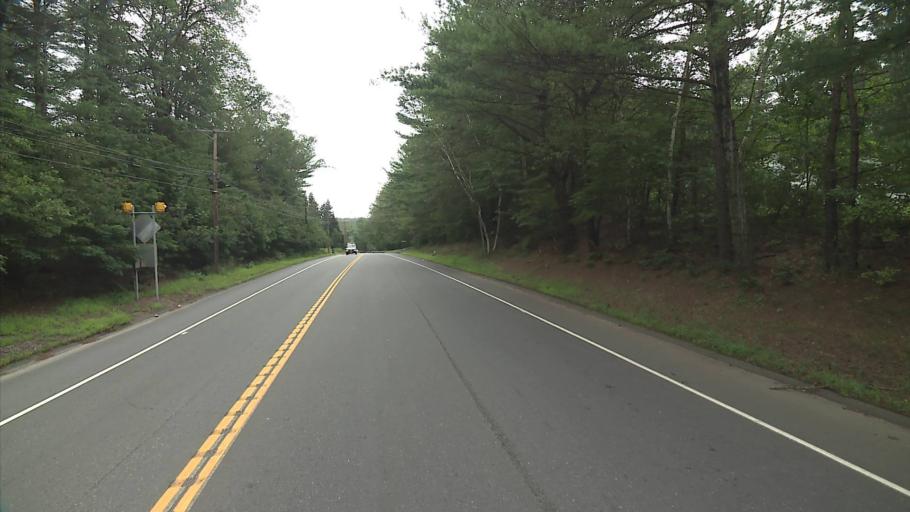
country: US
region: Connecticut
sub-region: Tolland County
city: Stafford Springs
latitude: 41.8816
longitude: -72.2923
